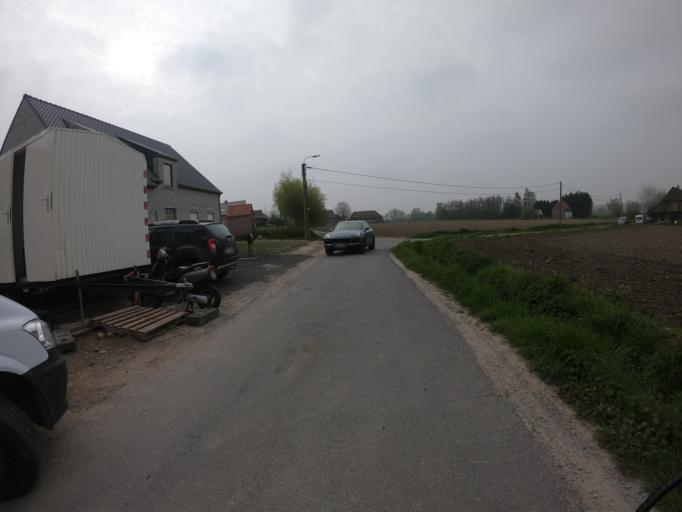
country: BE
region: Flanders
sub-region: Provincie West-Vlaanderen
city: Zwevegem
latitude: 50.8132
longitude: 3.3696
